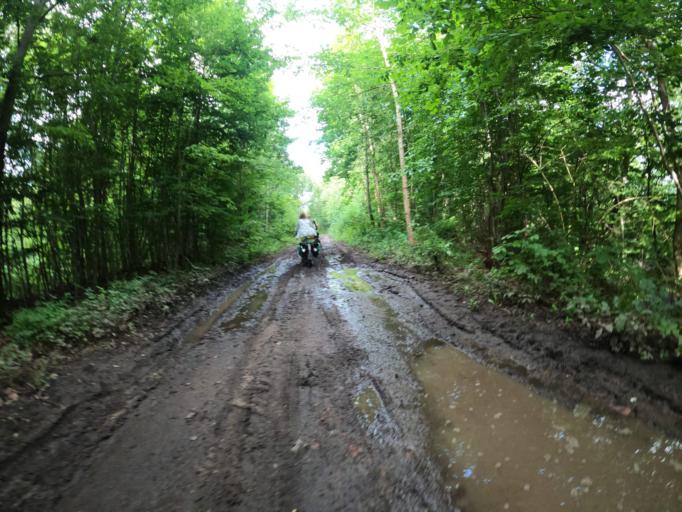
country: PL
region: West Pomeranian Voivodeship
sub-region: Powiat szczecinecki
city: Grzmiaca
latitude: 53.8753
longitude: 16.4679
